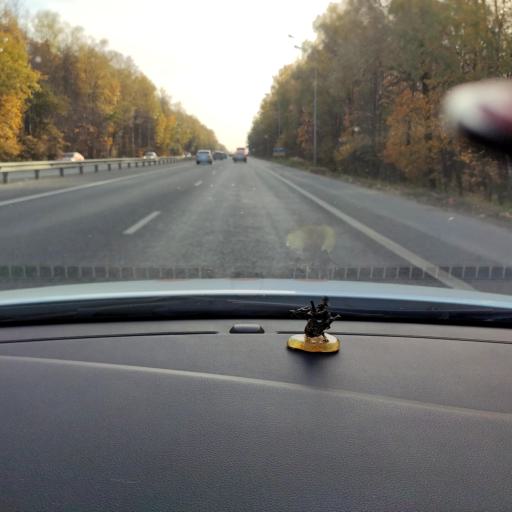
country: RU
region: Tatarstan
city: Osinovo
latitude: 55.8448
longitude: 48.8521
